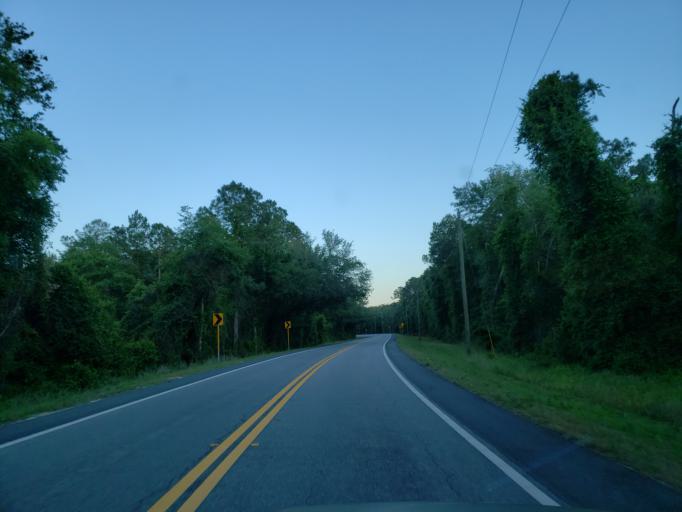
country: US
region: Georgia
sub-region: Echols County
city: Statenville
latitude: 30.5609
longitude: -83.1367
